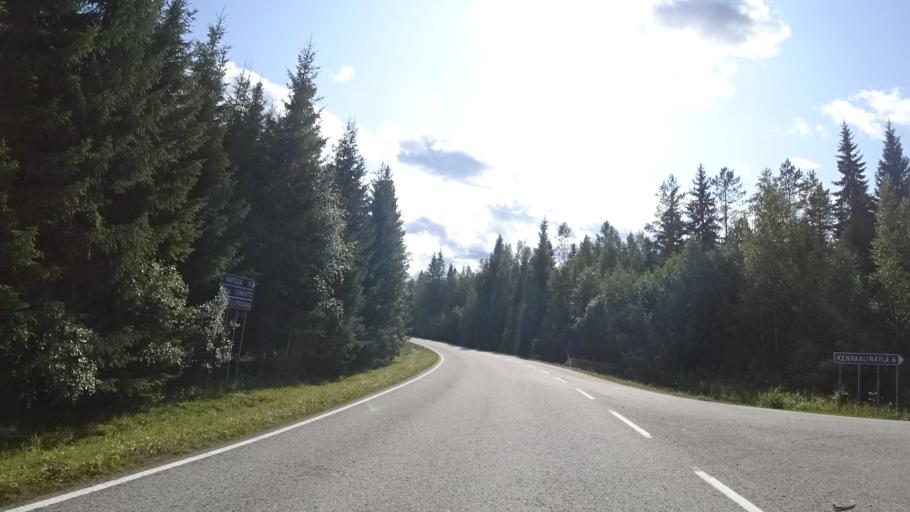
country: RU
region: Republic of Karelia
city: Vyartsilya
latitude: 62.2536
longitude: 30.7356
